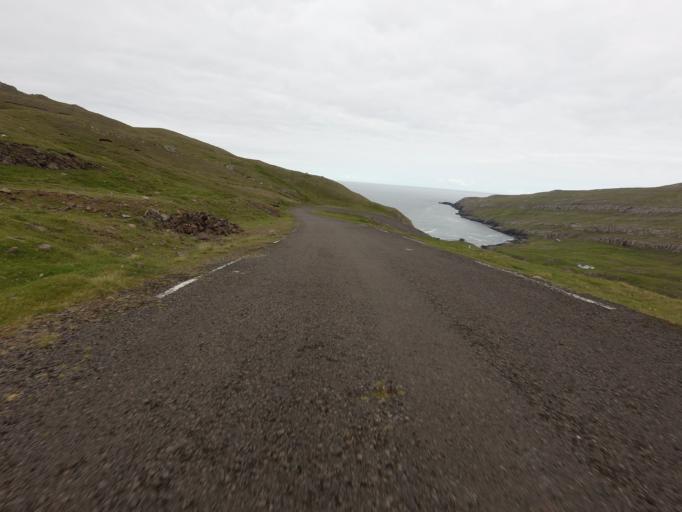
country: FO
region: Suduroy
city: Vagur
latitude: 61.4415
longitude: -6.7345
